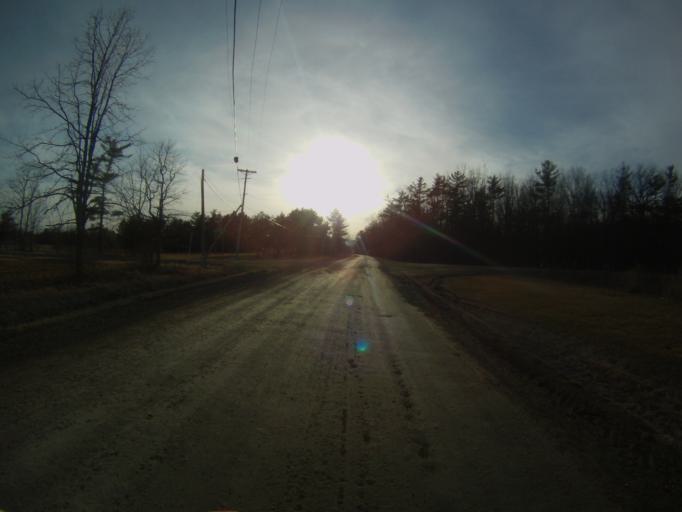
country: US
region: New York
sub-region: Essex County
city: Port Henry
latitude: 44.0267
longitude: -73.3410
